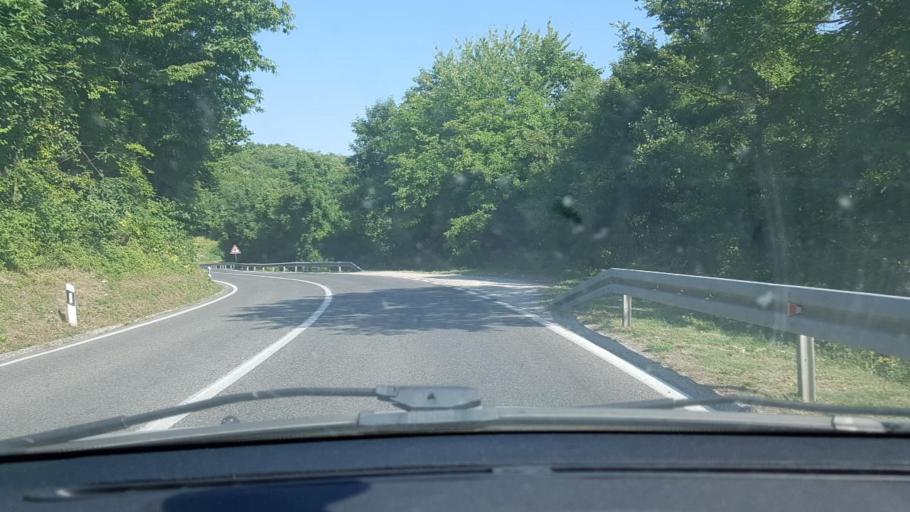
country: BA
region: Federation of Bosnia and Herzegovina
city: Skokovi
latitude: 45.0389
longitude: 15.9183
